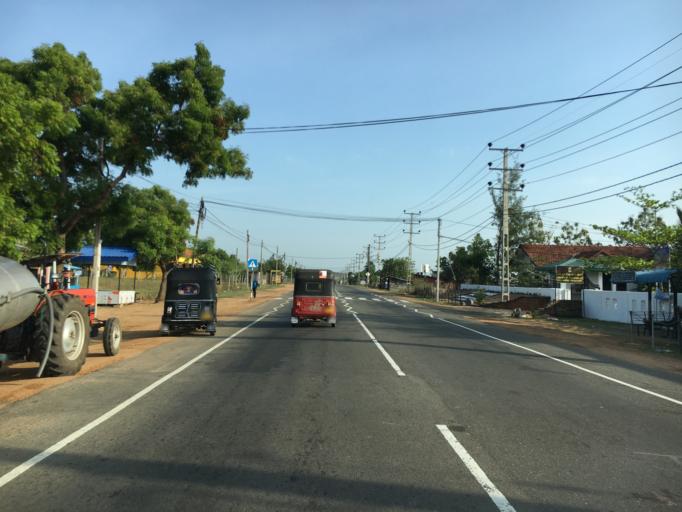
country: LK
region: Eastern Province
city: Eravur Town
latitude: 7.9314
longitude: 81.5118
